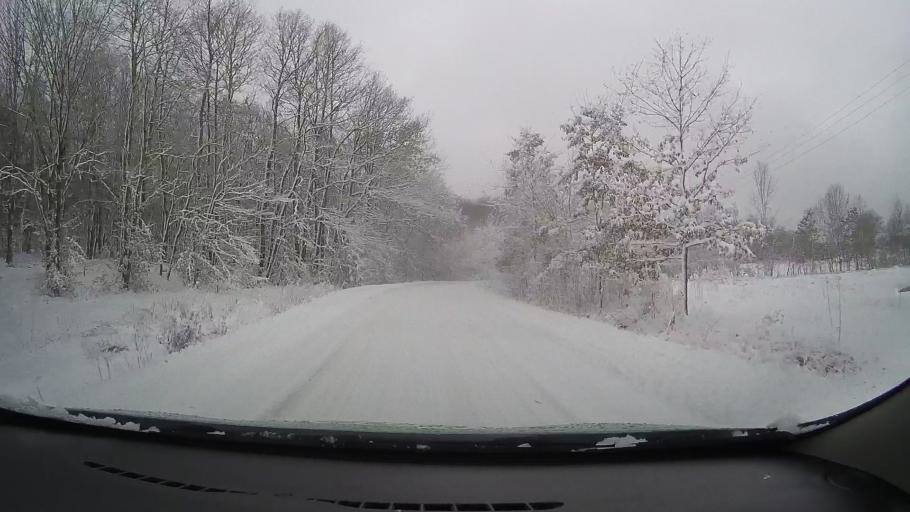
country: RO
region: Hunedoara
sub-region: Comuna Carjiti
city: Carjiti
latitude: 45.8425
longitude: 22.8538
